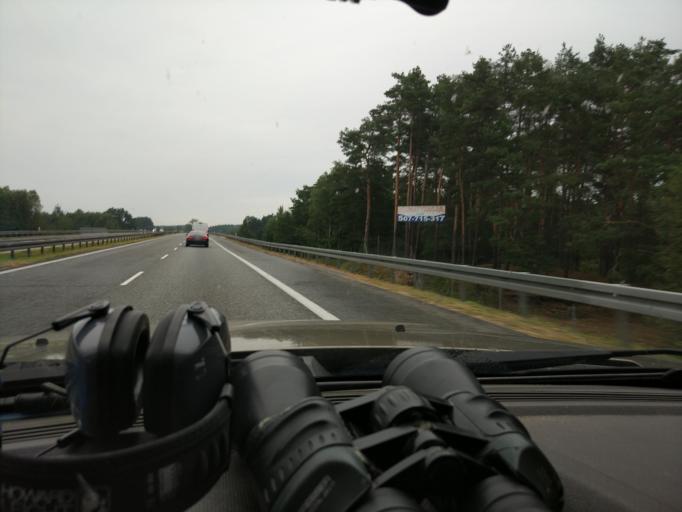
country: PL
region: Masovian Voivodeship
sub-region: Powiat wyszkowski
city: Wyszkow
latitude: 52.5438
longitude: 21.4394
